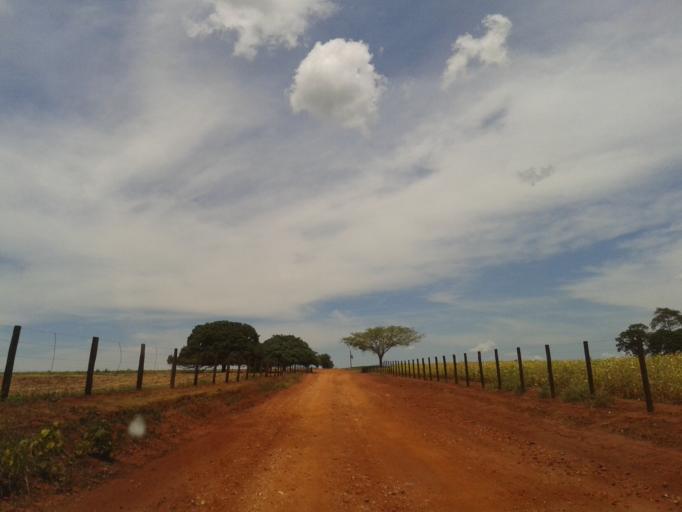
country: BR
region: Minas Gerais
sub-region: Capinopolis
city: Capinopolis
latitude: -18.7077
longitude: -49.7130
